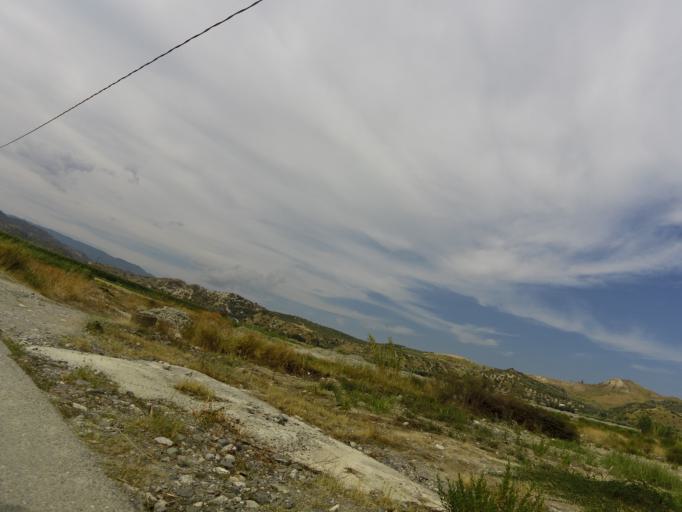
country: IT
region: Calabria
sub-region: Provincia di Reggio Calabria
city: Monasterace
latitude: 38.4510
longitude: 16.5202
